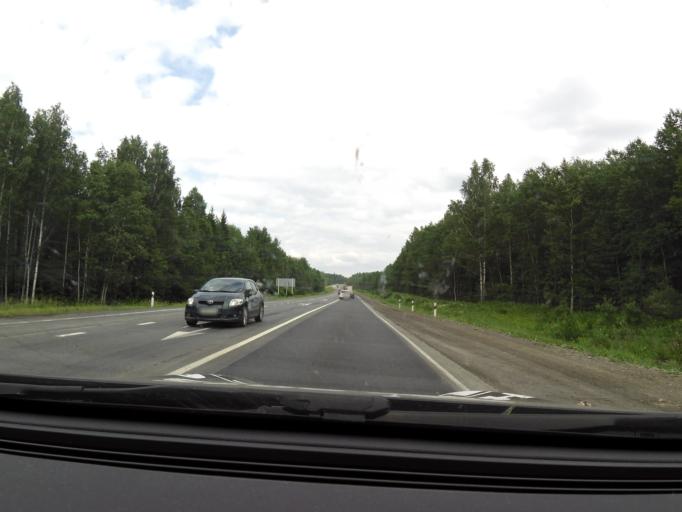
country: RU
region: Sverdlovsk
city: Druzhinino
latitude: 56.8466
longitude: 59.6834
